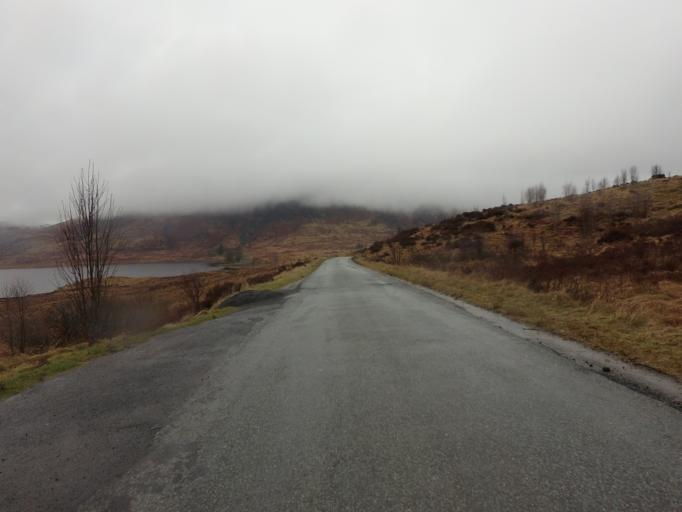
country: GB
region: Scotland
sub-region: West Dunbartonshire
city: Balloch
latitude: 56.2468
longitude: -4.5847
